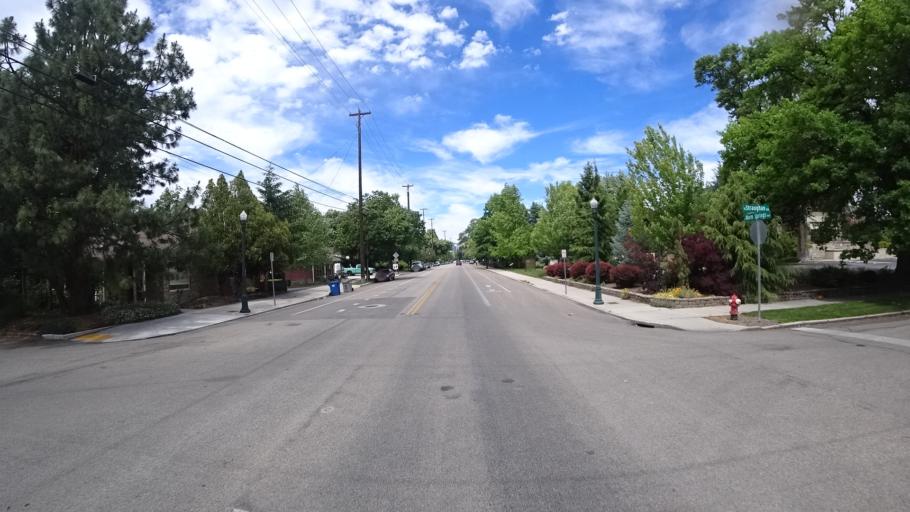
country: US
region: Idaho
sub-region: Ada County
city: Boise
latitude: 43.6087
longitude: -116.1863
